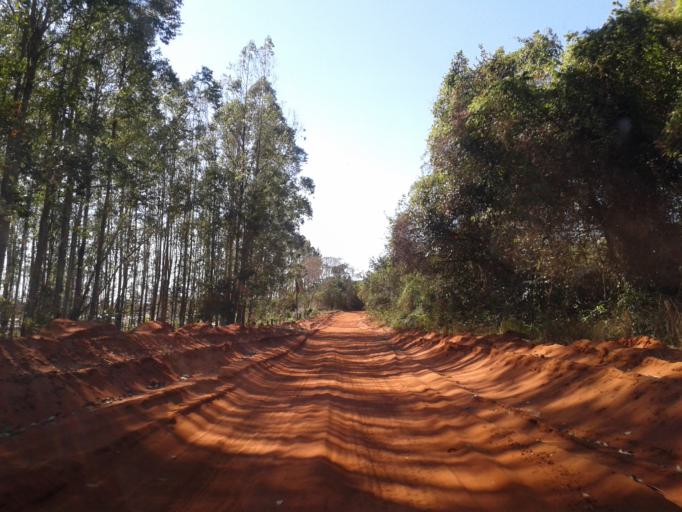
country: BR
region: Minas Gerais
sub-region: Ituiutaba
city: Ituiutaba
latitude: -19.0352
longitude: -49.3063
